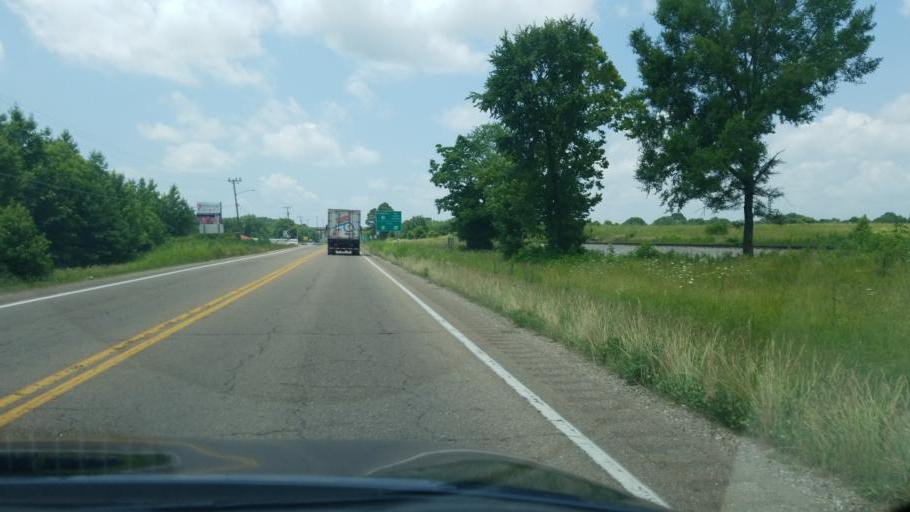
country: US
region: Tennessee
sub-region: Carroll County
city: Huntingdon
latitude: 36.0131
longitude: -88.3893
